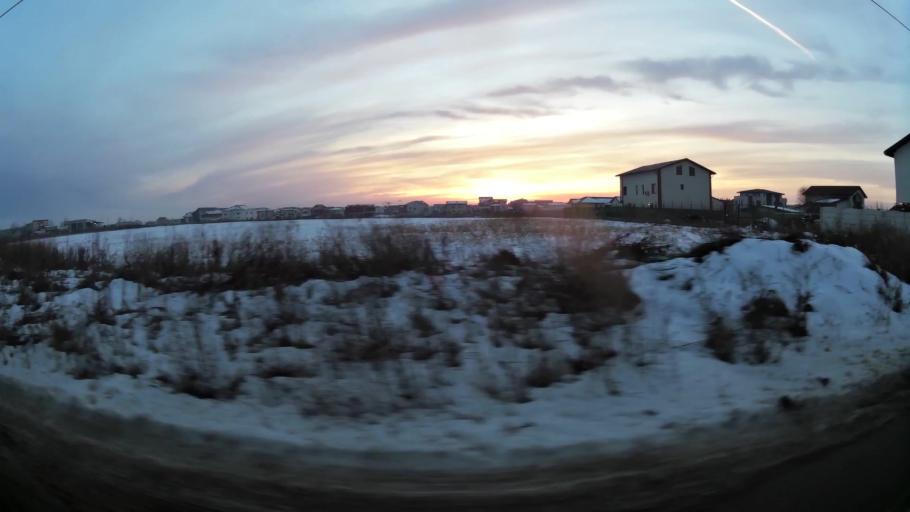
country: RO
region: Ilfov
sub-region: Comuna Magurele
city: Magurele
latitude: 44.3853
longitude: 26.0235
